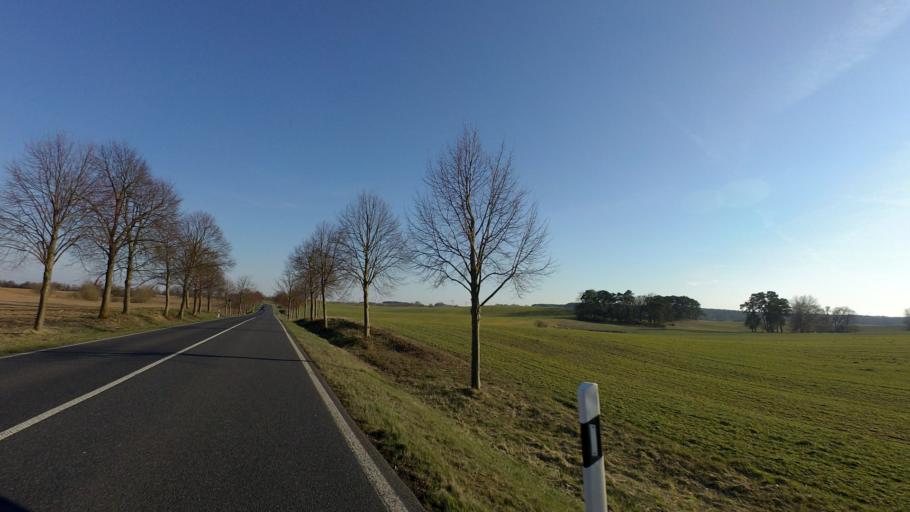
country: DE
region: Brandenburg
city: Althuttendorf
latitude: 52.9297
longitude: 13.7914
